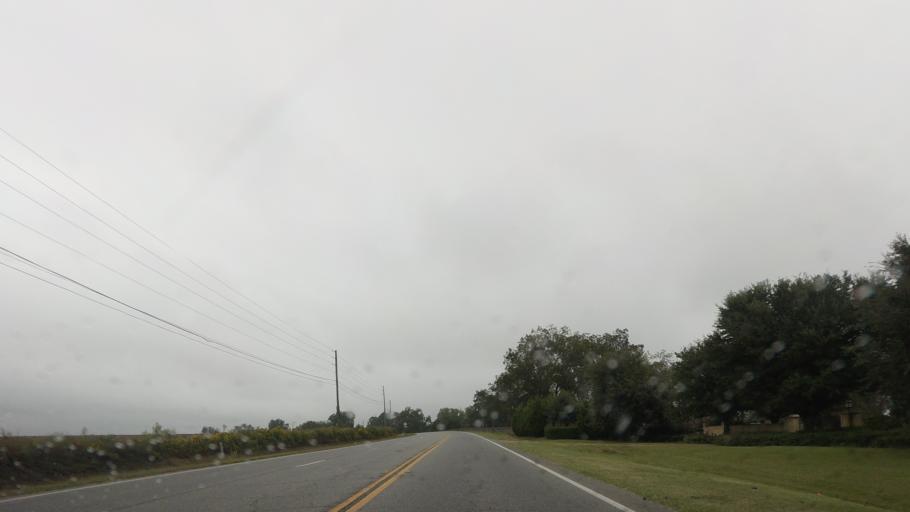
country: US
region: Georgia
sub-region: Ben Hill County
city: Fitzgerald
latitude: 31.6800
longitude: -83.2370
